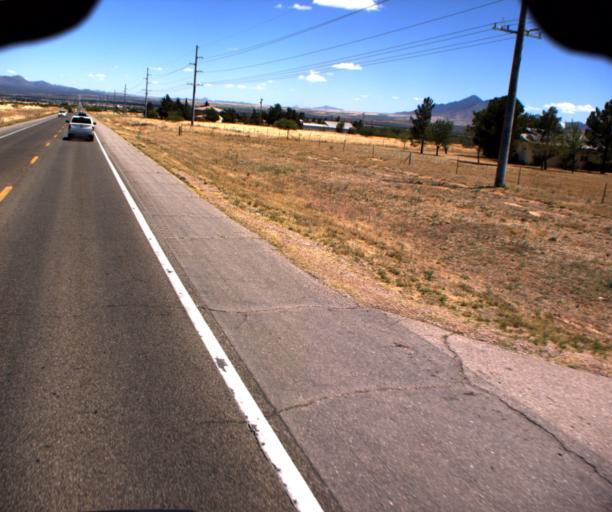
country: US
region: Arizona
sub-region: Cochise County
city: Sierra Vista Southeast
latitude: 31.3799
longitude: -110.1927
